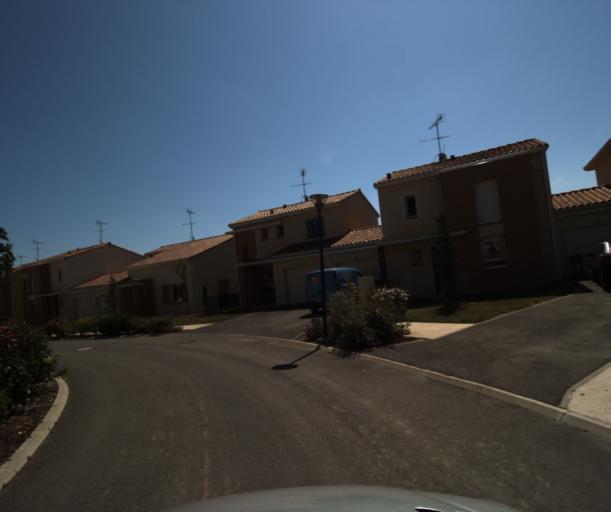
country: FR
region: Midi-Pyrenees
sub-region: Departement de la Haute-Garonne
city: Eaunes
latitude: 43.4225
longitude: 1.3526
